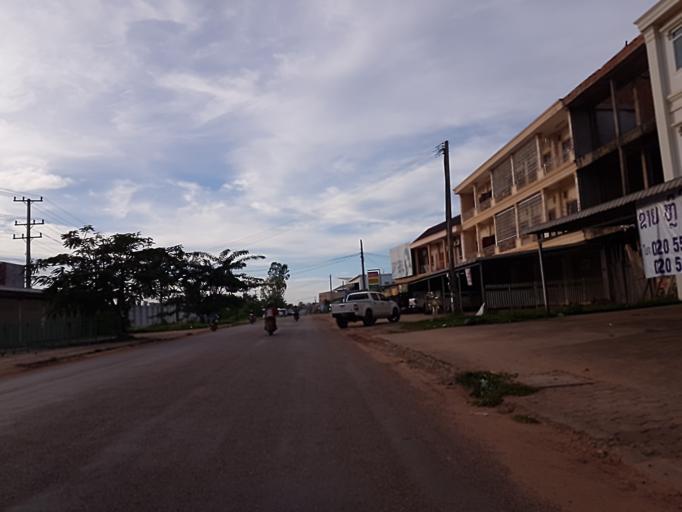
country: TH
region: Nong Khai
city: Si Chiang Mai
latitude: 18.0037
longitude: 102.5564
